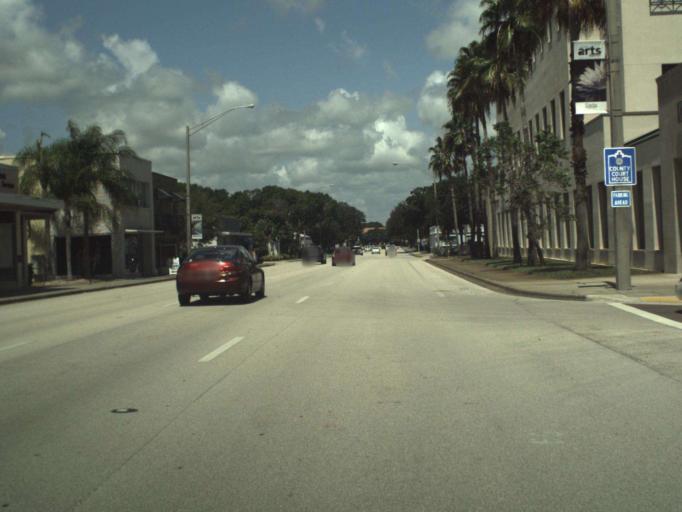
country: US
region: Florida
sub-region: Indian River County
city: Vero Beach
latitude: 27.6387
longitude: -80.4003
